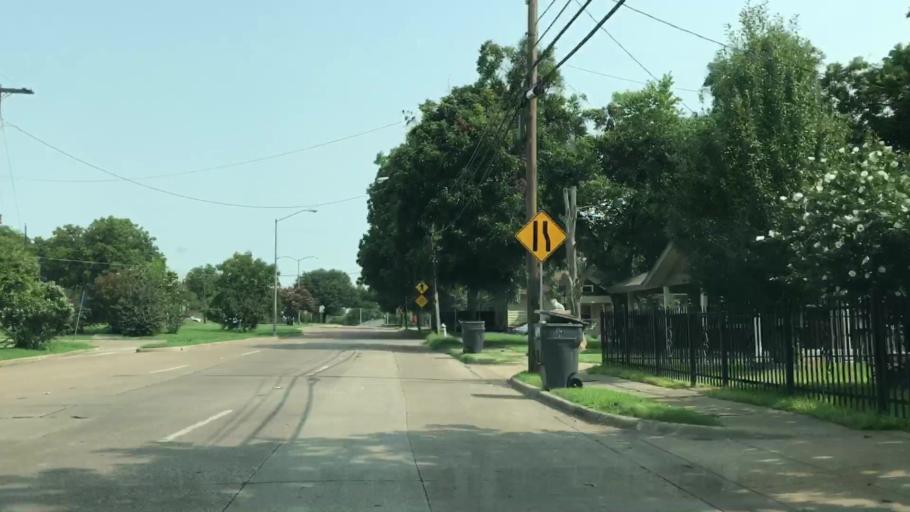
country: US
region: Texas
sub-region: Dallas County
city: Dallas
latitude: 32.7510
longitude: -96.8375
